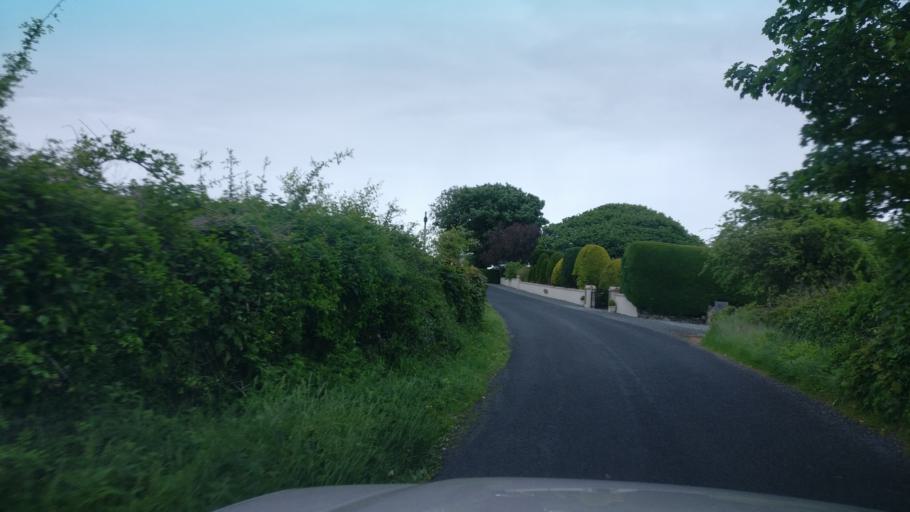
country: IE
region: Connaught
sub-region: County Galway
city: Loughrea
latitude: 53.1167
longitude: -8.4342
